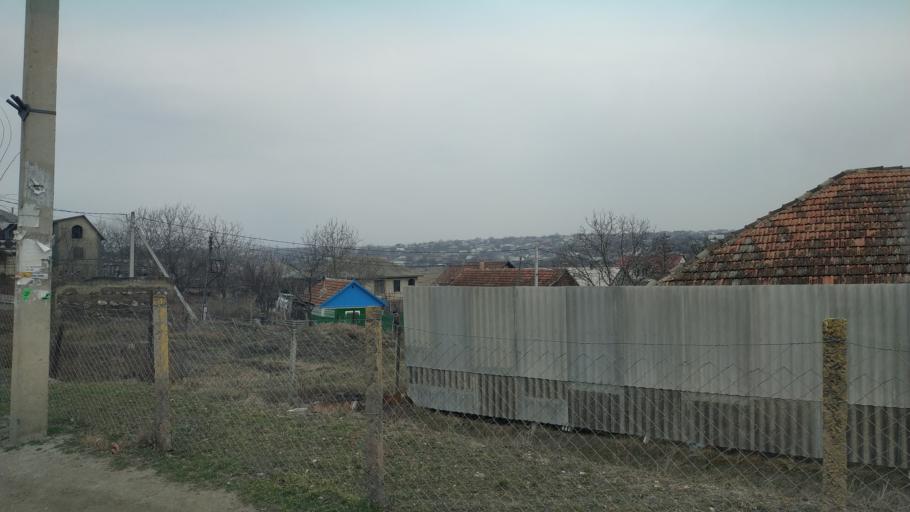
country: MD
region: Chisinau
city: Singera
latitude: 46.9099
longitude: 28.9669
